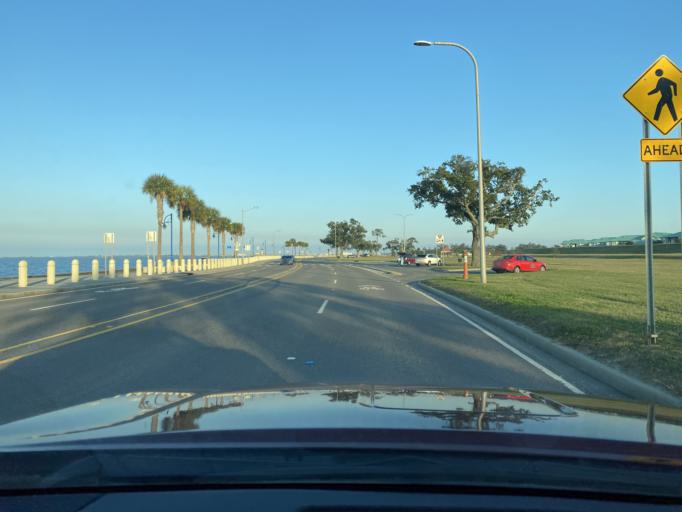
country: US
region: Louisiana
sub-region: Orleans Parish
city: New Orleans
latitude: 30.0348
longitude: -90.0488
